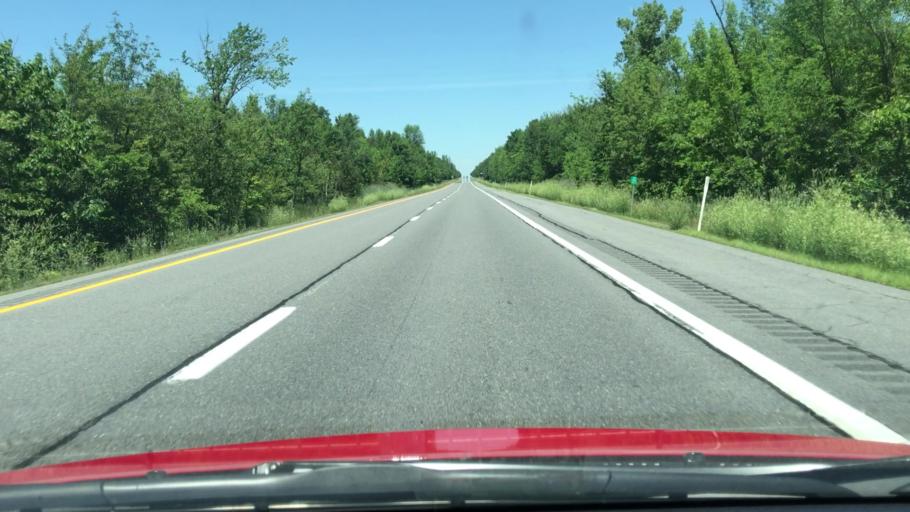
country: US
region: New York
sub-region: Clinton County
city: Champlain
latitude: 44.9475
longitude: -73.4479
